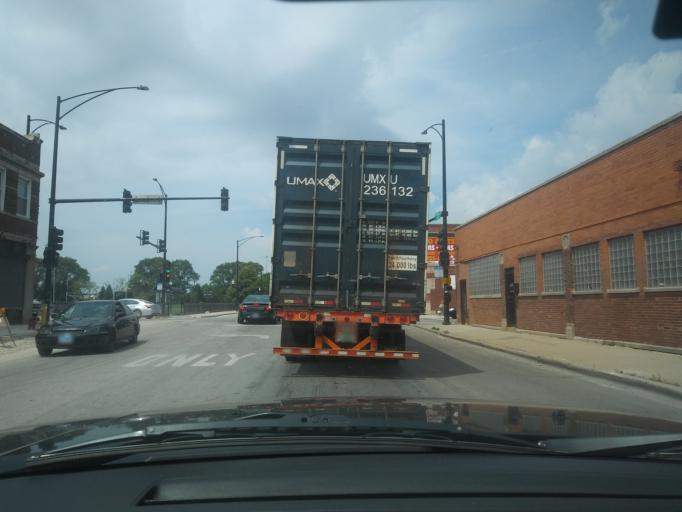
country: US
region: Illinois
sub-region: Cook County
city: Chicago
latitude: 41.7867
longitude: -87.6737
